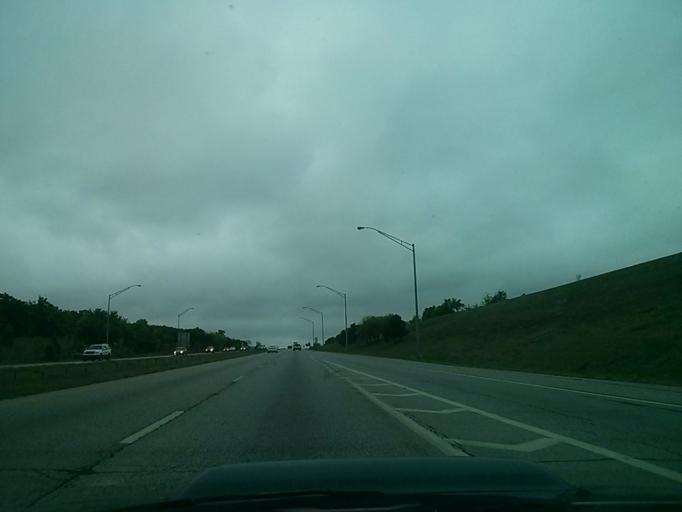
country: US
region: Oklahoma
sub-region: Tulsa County
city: Oakhurst
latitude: 36.0846
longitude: -96.0068
